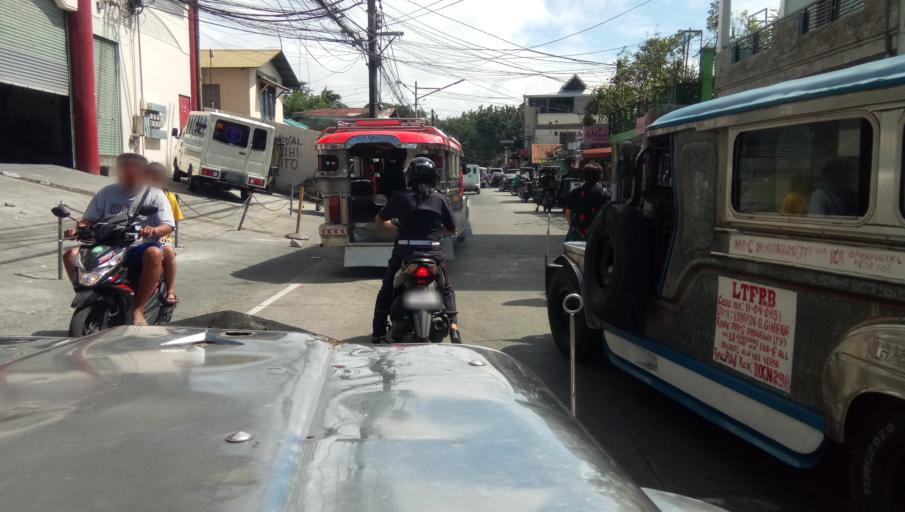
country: PH
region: Calabarzon
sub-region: Province of Cavite
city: Dasmarinas
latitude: 14.3262
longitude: 120.9353
